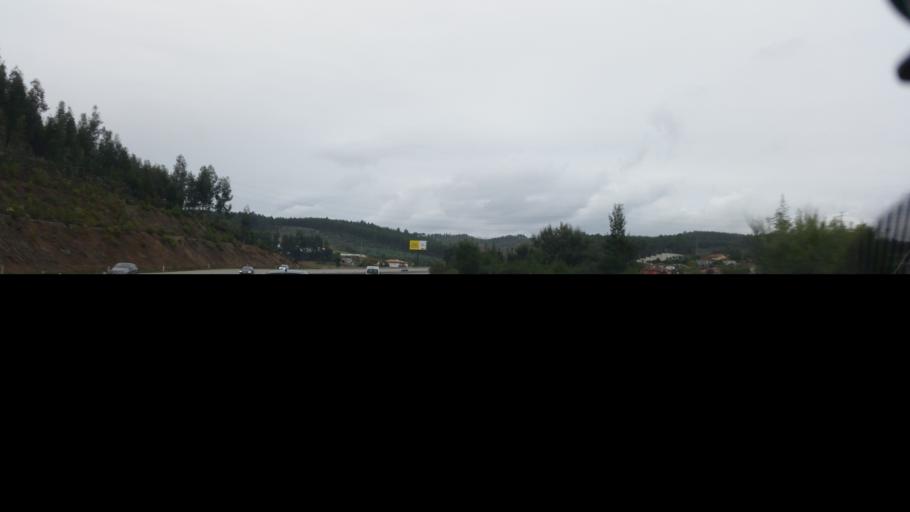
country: PT
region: Porto
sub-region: Trofa
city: Sao Romao do Coronado
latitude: 41.2994
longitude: -8.5382
